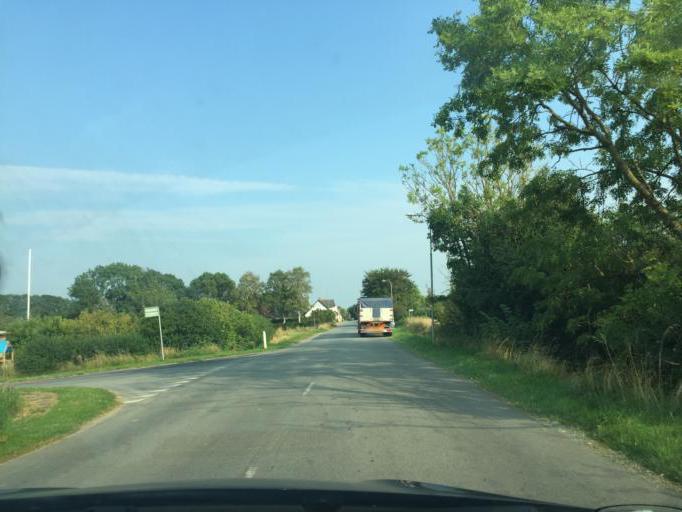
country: DK
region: South Denmark
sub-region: Faaborg-Midtfyn Kommune
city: Arslev
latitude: 55.2825
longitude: 10.4882
